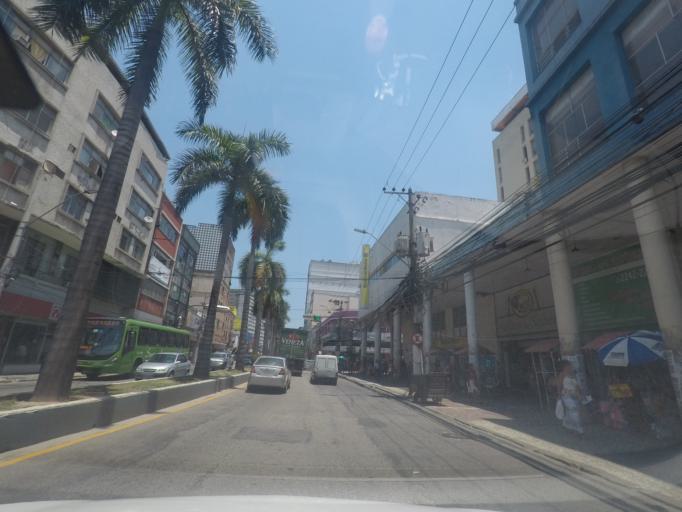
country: BR
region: Rio de Janeiro
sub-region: Duque De Caxias
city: Duque de Caxias
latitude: -22.7895
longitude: -43.3103
